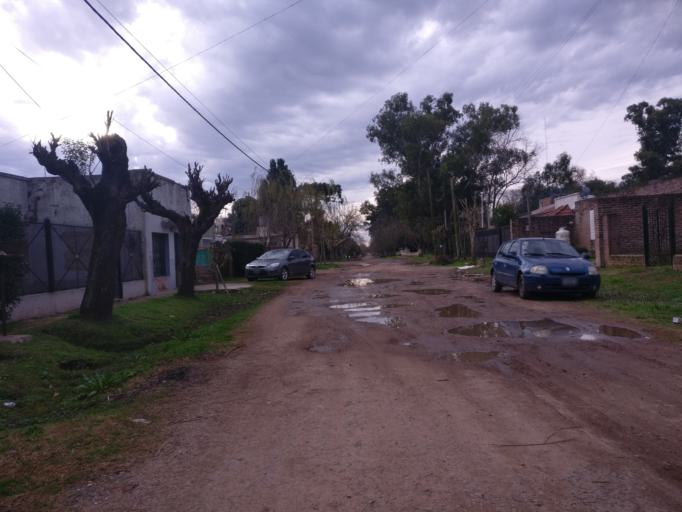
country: AR
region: Buenos Aires
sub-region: Partido de Ezeiza
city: Ezeiza
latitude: -34.9400
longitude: -58.6127
